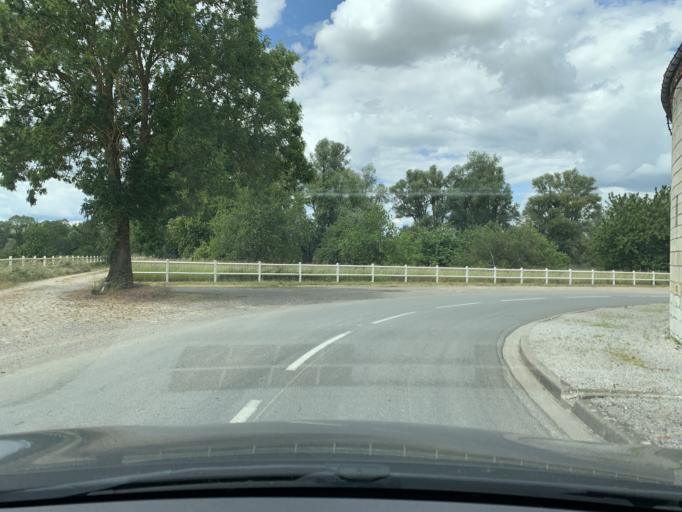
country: FR
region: Nord-Pas-de-Calais
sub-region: Departement du Nord
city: Masnieres
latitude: 50.0776
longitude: 3.2231
